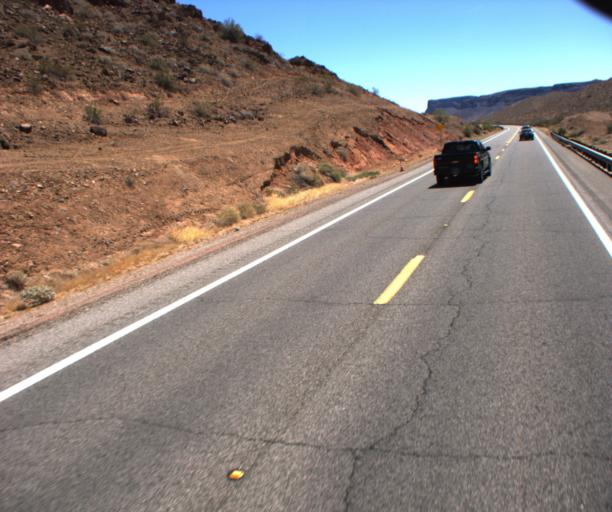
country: US
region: Arizona
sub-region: La Paz County
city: Cienega Springs
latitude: 34.3308
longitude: -114.1346
